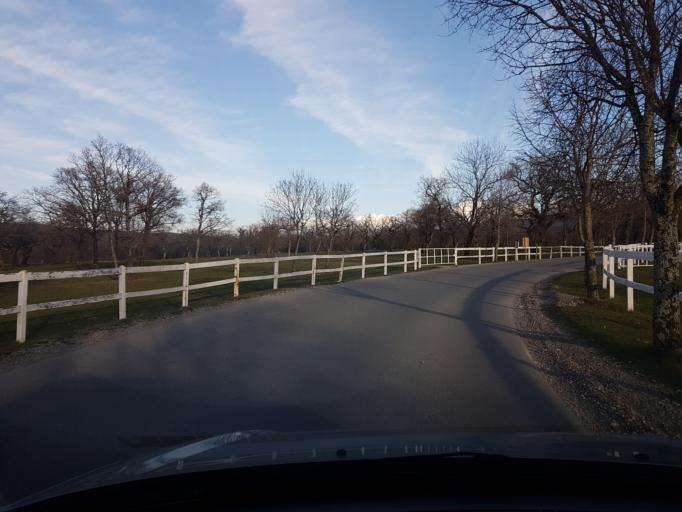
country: SI
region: Sezana
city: Sezana
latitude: 45.6700
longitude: 13.8874
